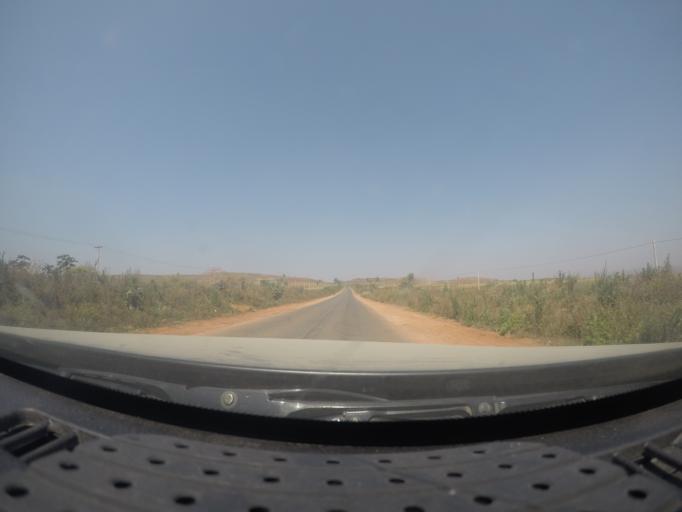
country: MM
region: Shan
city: Taunggyi
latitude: 20.8060
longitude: 96.6217
